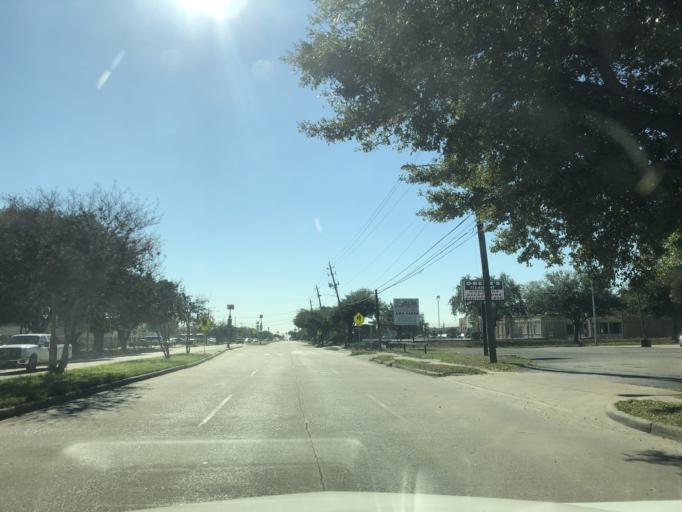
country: US
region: Texas
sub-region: Harris County
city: Houston
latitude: 29.8211
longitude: -95.3021
